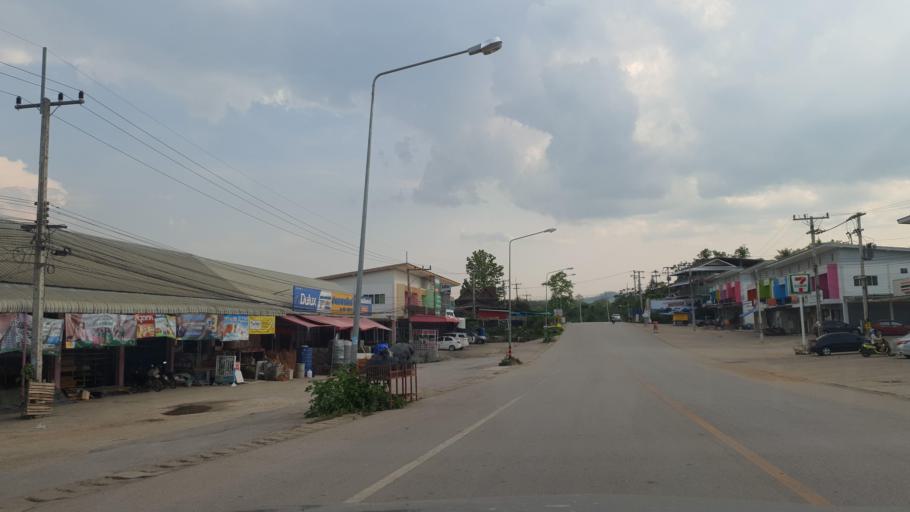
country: TH
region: Chiang Mai
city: Pai
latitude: 19.3479
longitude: 98.4344
